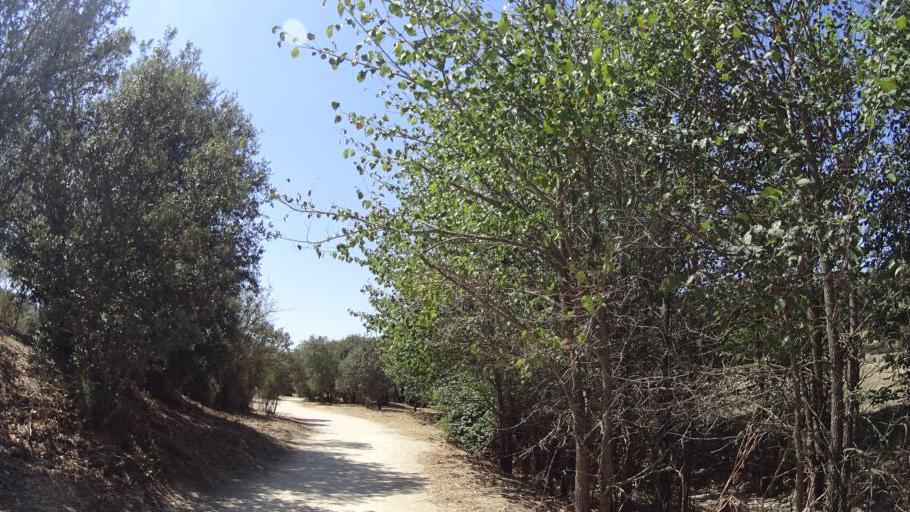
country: ES
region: Madrid
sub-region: Provincia de Madrid
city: Boadilla del Monte
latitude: 40.4100
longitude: -3.8689
